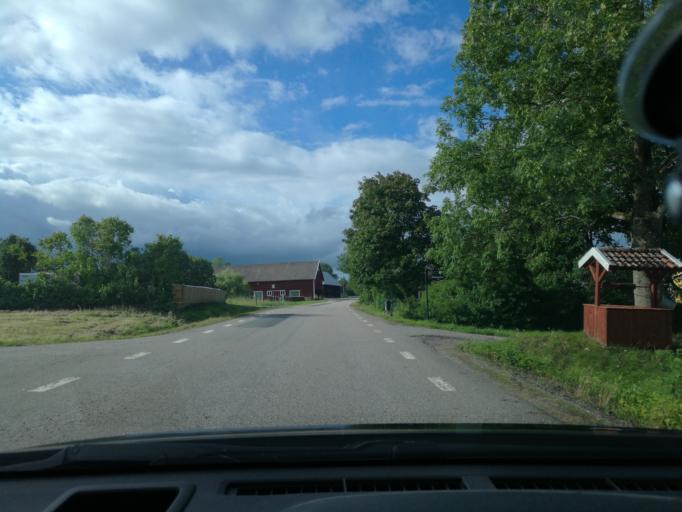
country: SE
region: Kronoberg
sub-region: Vaxjo Kommun
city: Braas
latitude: 57.1108
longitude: 14.9785
